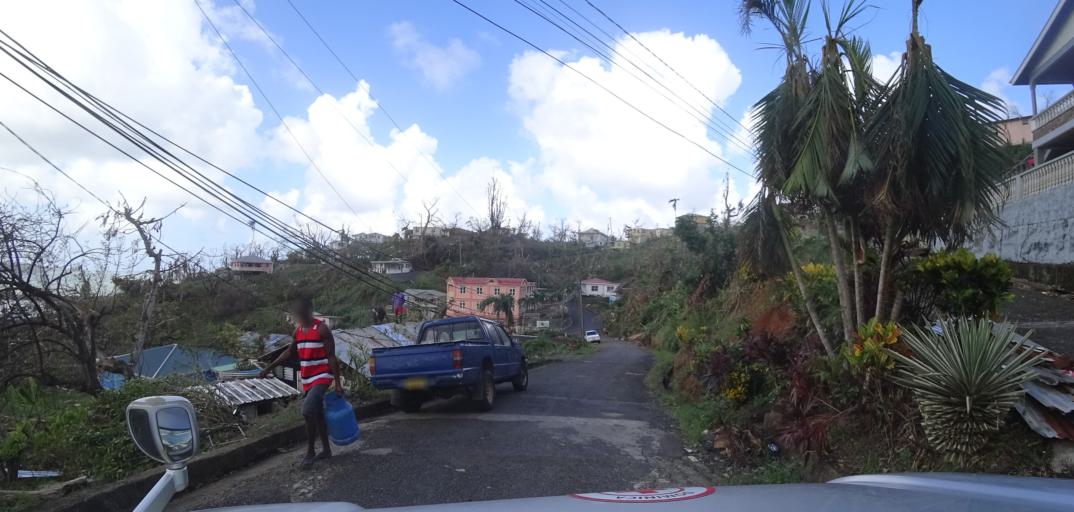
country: DM
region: Saint Andrew
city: Marigot
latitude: 15.5391
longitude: -61.2849
